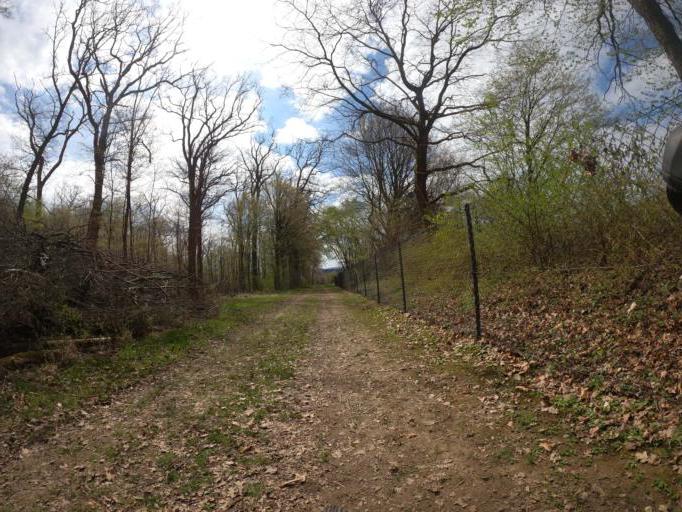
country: DE
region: Baden-Wuerttemberg
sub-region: Tuebingen Region
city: Wannweil
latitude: 48.5024
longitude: 9.1375
